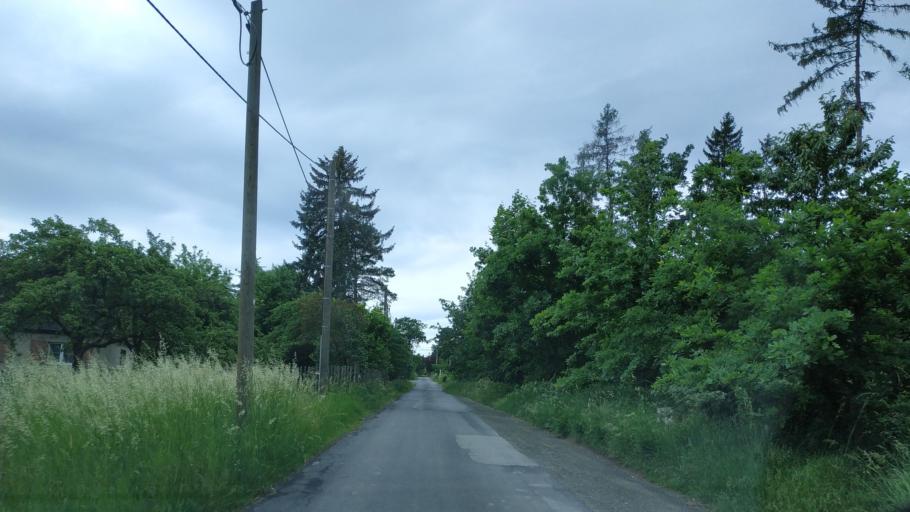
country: DE
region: Saxony
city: Syrau
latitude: 50.5371
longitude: 12.1202
